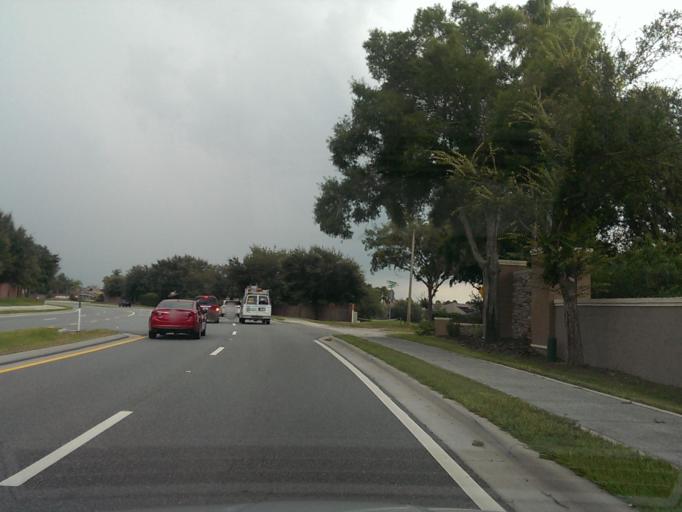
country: US
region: Florida
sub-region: Orange County
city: Lake Butler
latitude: 28.5098
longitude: -81.5845
